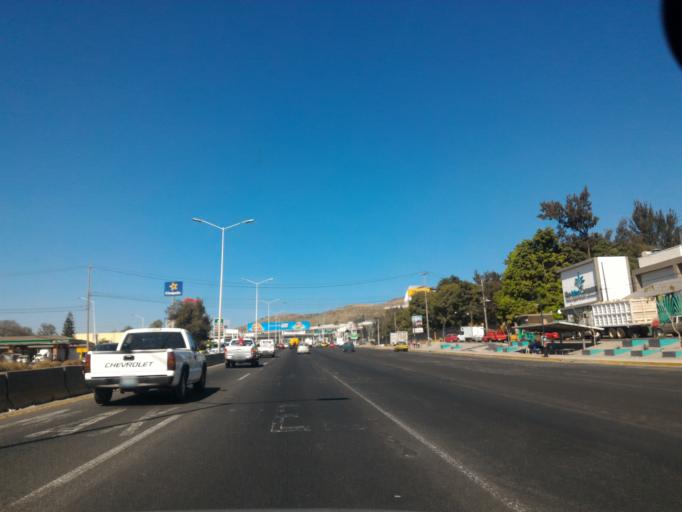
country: MX
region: Jalisco
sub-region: San Pedro Tlaquepaque
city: Paseo del Prado
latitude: 20.6025
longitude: -103.3996
